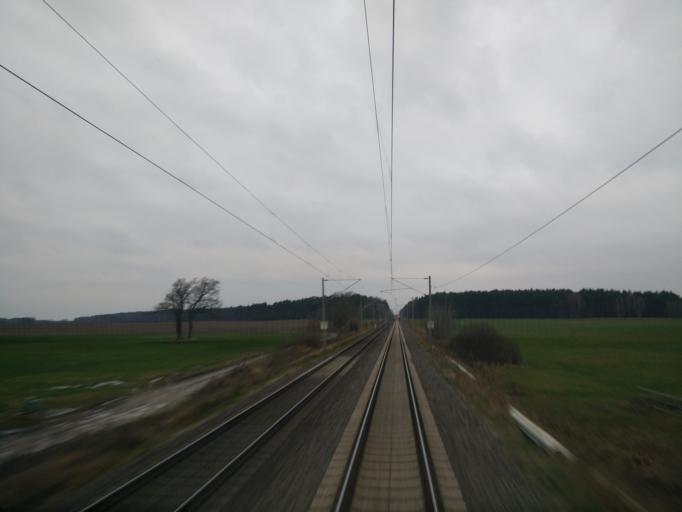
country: DE
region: Mecklenburg-Vorpommern
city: Grabow
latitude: 53.2643
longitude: 11.6029
